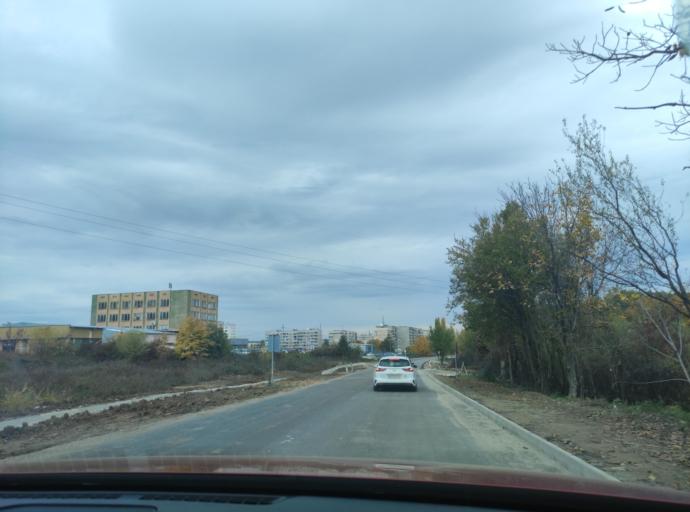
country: BG
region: Montana
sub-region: Obshtina Montana
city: Montana
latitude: 43.3940
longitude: 23.2408
